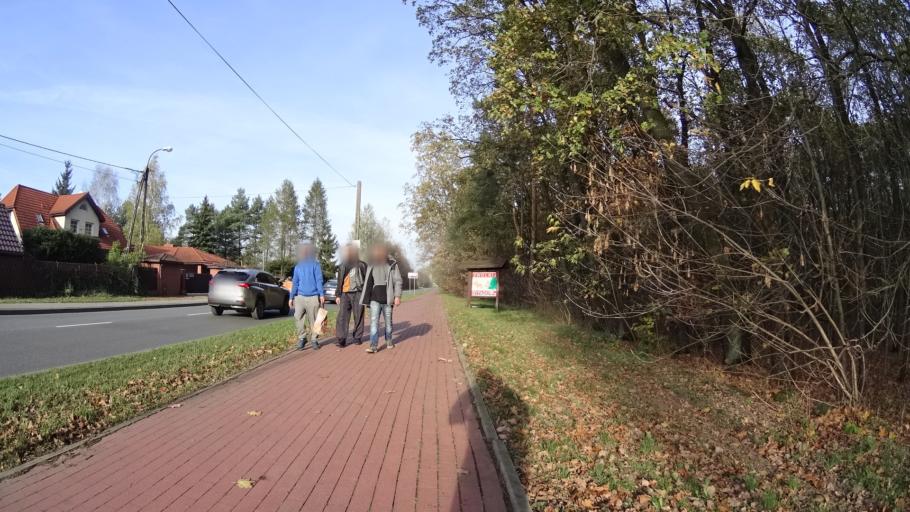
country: PL
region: Masovian Voivodeship
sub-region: Powiat warszawski zachodni
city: Babice
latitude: 52.2658
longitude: 20.8580
